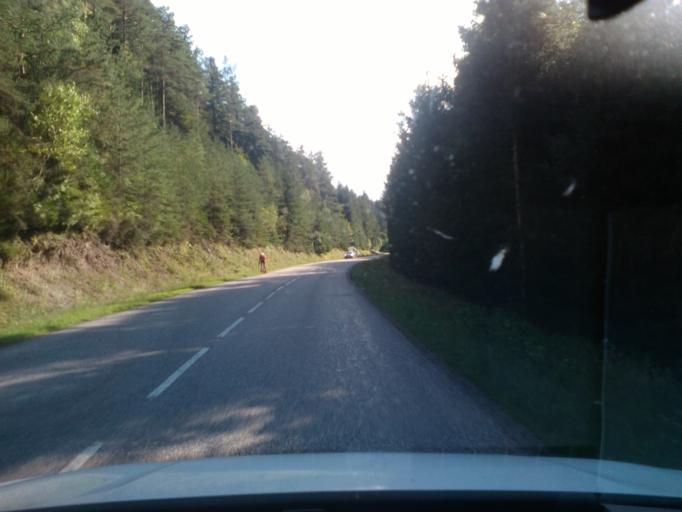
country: FR
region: Lorraine
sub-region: Departement des Vosges
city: Taintrux
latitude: 48.2229
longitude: 6.9036
